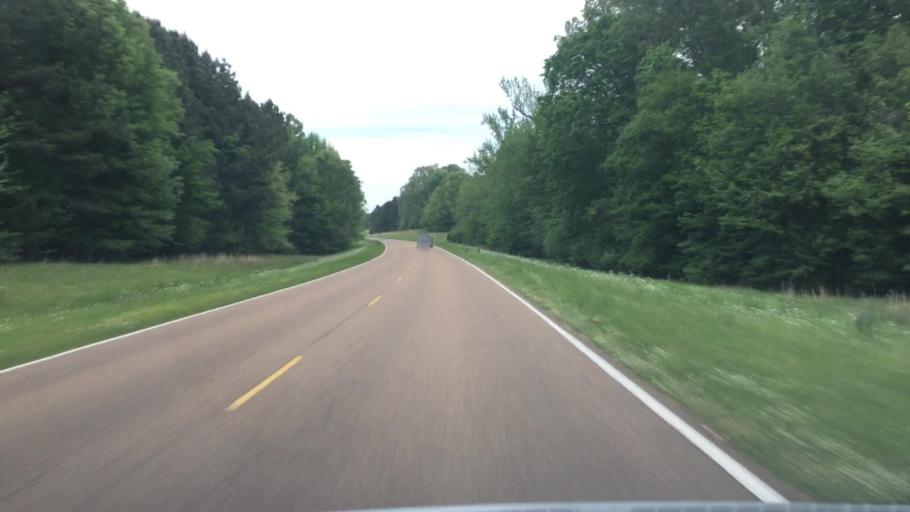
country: US
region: Mississippi
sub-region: Hinds County
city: Clinton
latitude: 32.3906
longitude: -90.2525
